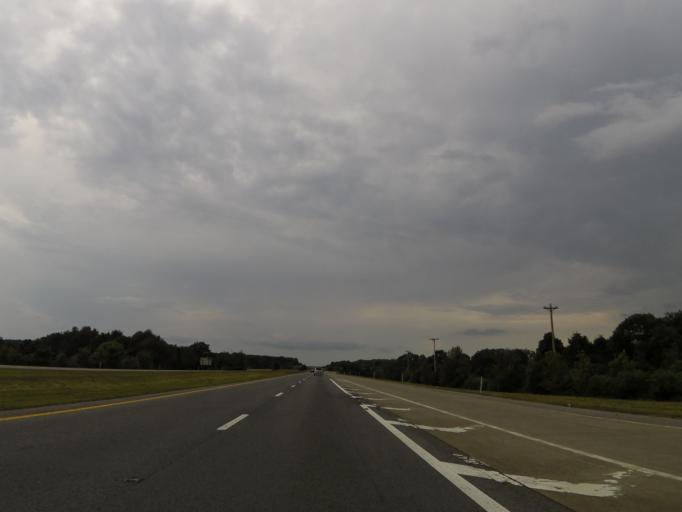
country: US
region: Tennessee
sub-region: Rutherford County
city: Smyrna
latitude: 35.9826
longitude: -86.4407
